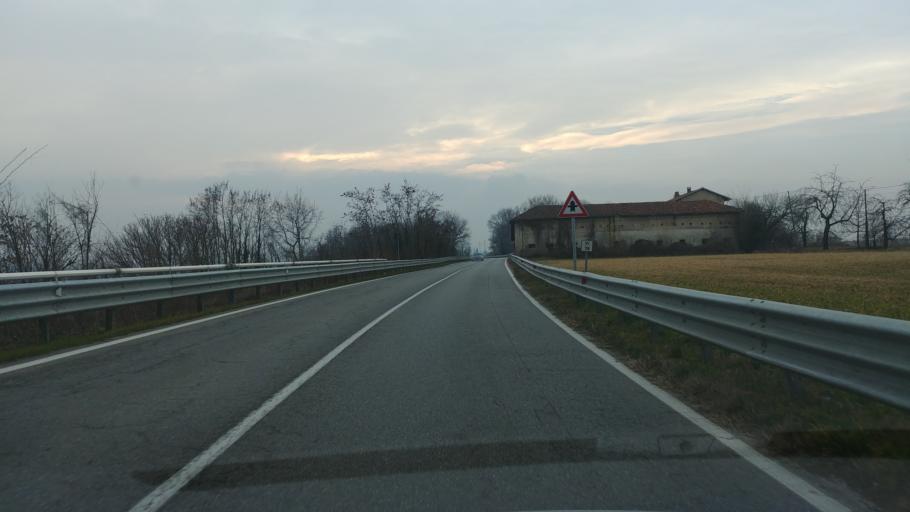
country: IT
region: Piedmont
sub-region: Provincia di Cuneo
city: Castelletto Stura
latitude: 44.4488
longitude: 7.6177
